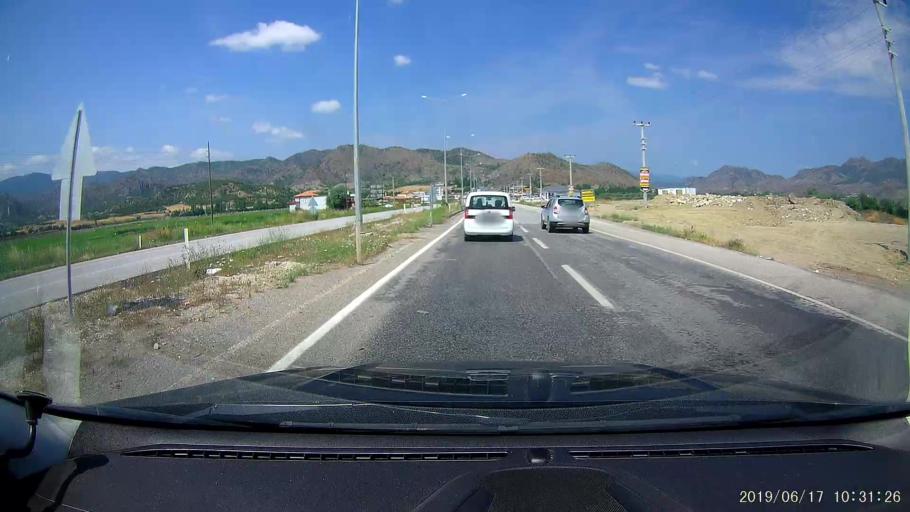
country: TR
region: Corum
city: Osmancik
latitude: 40.9789
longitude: 34.7871
